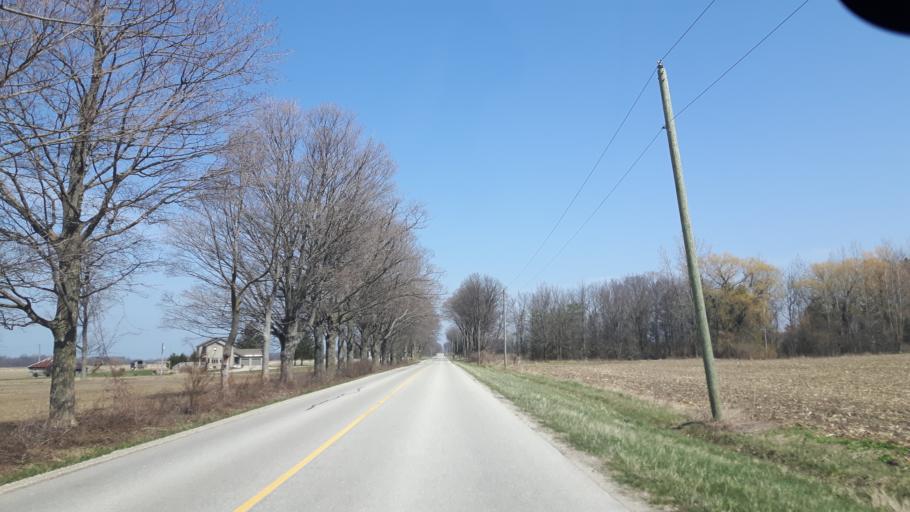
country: CA
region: Ontario
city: Goderich
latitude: 43.6915
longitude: -81.6848
